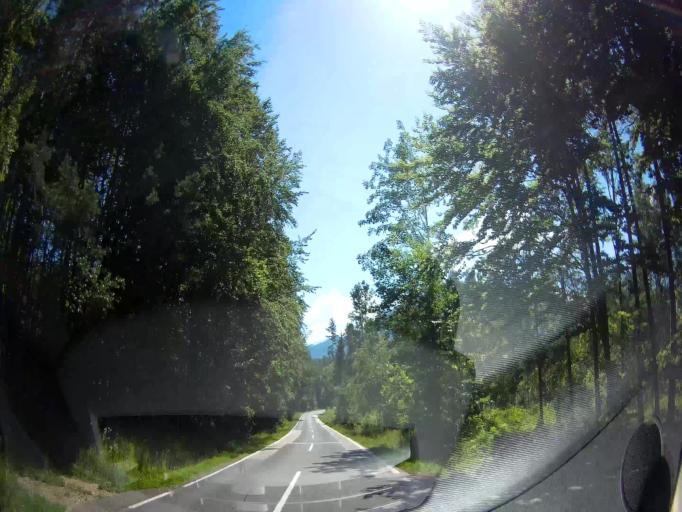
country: AT
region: Carinthia
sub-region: Politischer Bezirk Volkermarkt
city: Sittersdorf
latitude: 46.5381
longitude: 14.5746
